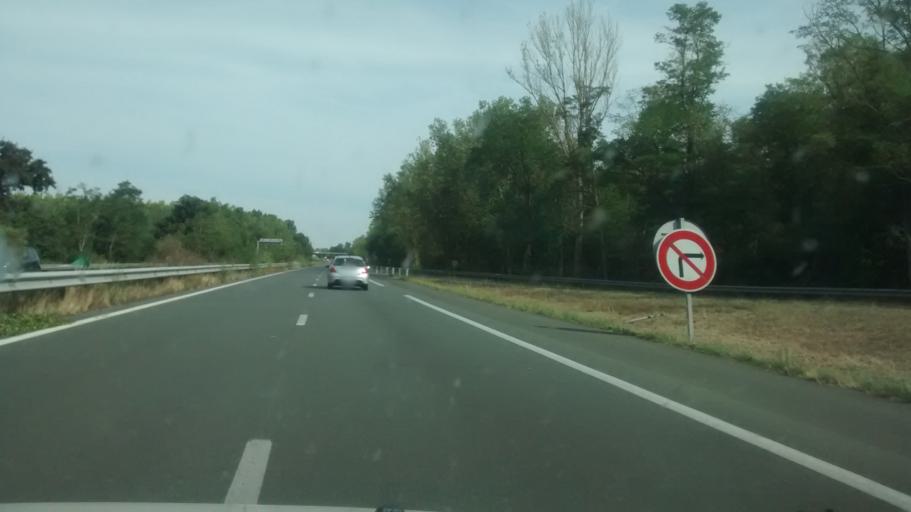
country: FR
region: Aquitaine
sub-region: Departement du Lot-et-Garonne
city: Damazan
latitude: 44.3453
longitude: 0.2506
